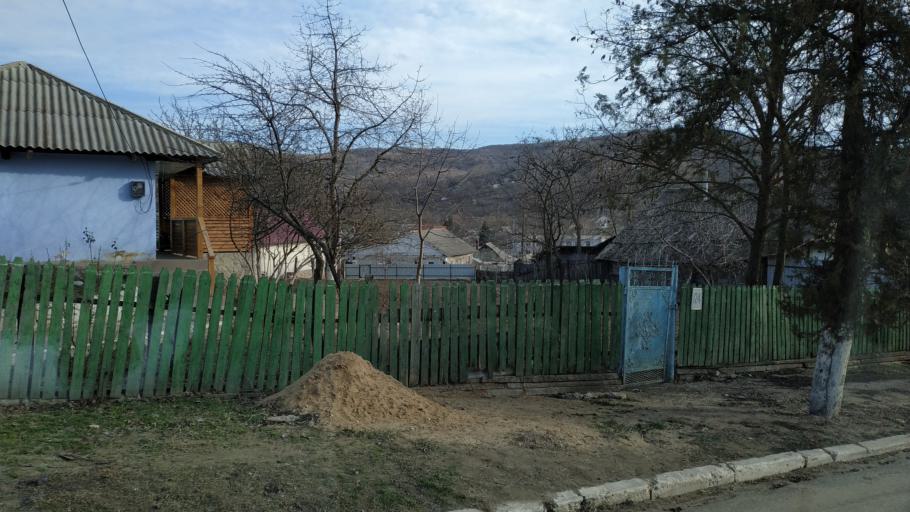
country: MD
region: Nisporeni
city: Nisporeni
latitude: 47.0824
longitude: 28.1883
